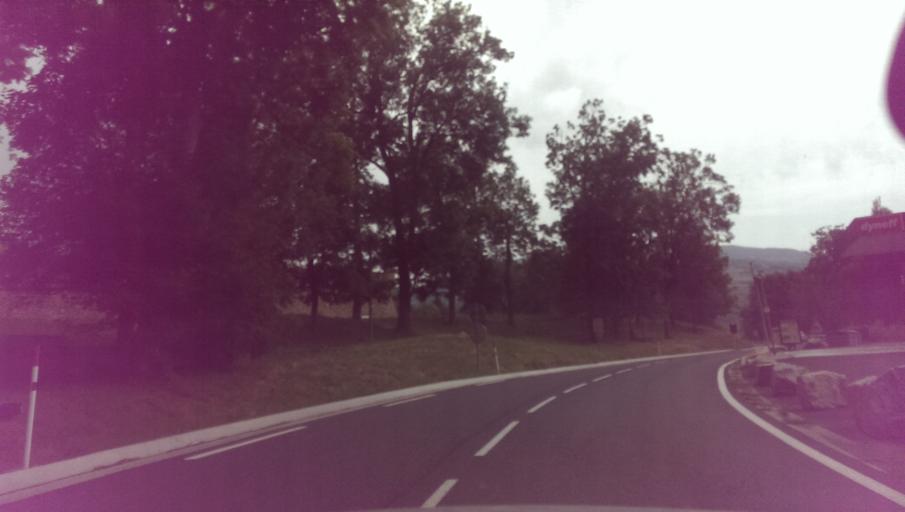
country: ES
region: Catalonia
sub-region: Provincia de Girona
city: Llivia
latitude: 42.5070
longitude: 2.1231
